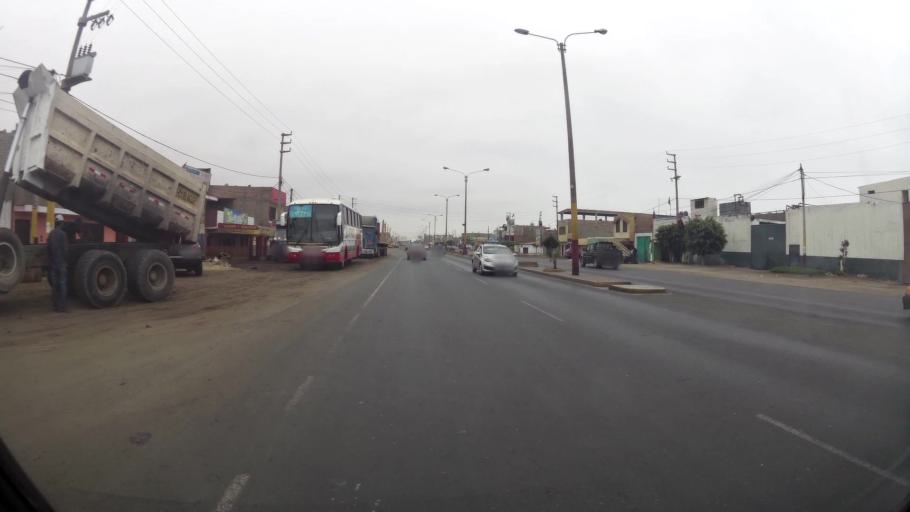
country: PE
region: Ancash
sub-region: Provincia de Santa
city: Chimbote
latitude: -9.0876
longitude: -78.5746
